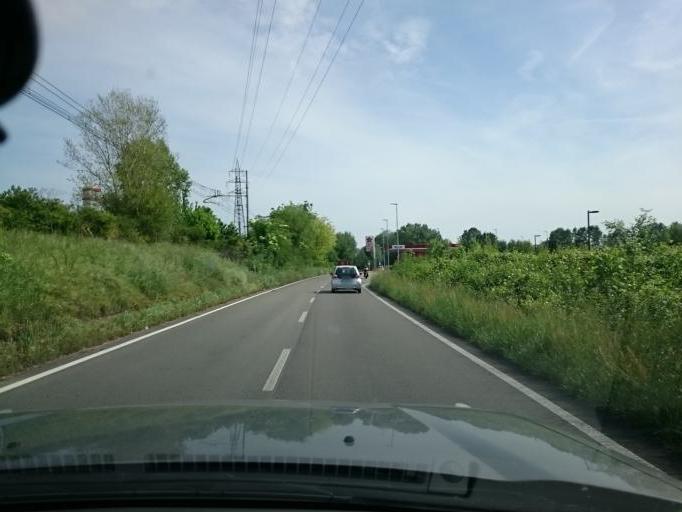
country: IT
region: Veneto
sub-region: Provincia di Padova
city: Padova
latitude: 45.4103
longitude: 11.9181
